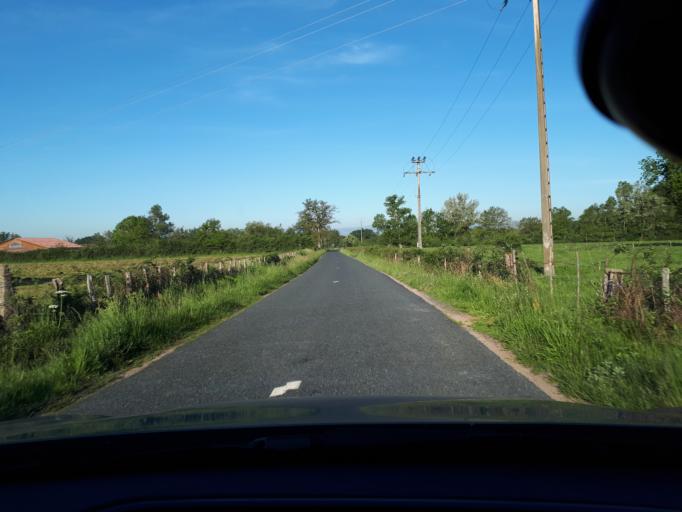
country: FR
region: Rhone-Alpes
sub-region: Departement de la Loire
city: Civens
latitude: 45.7571
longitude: 4.2504
